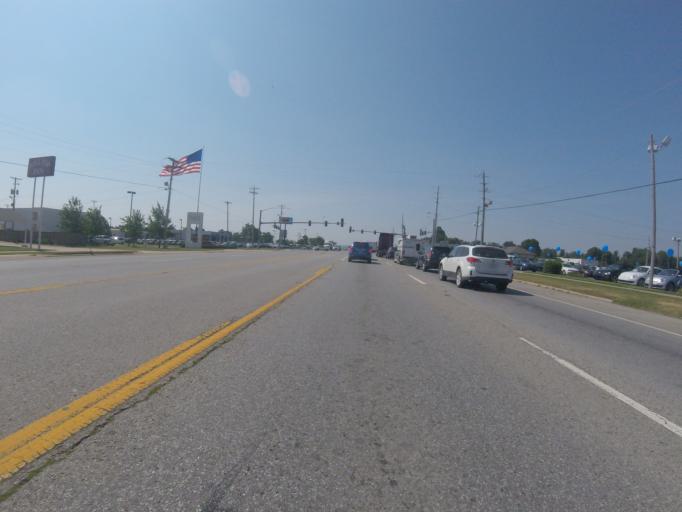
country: US
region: Arkansas
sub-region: Washington County
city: Johnson
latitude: 36.1531
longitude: -94.1440
